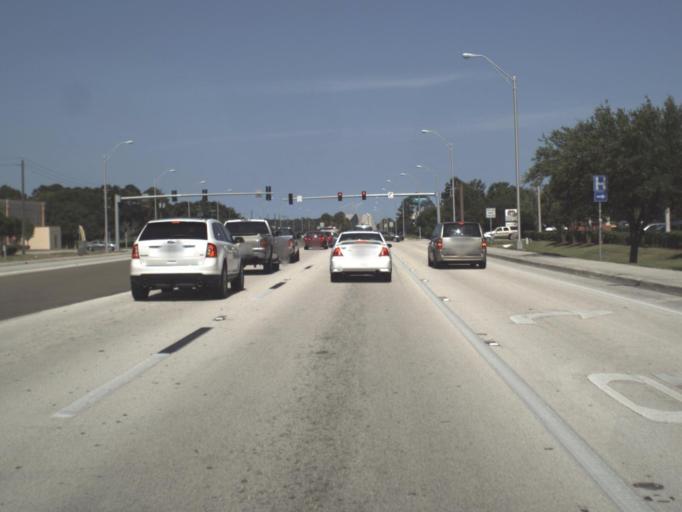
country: US
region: Florida
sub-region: Saint Johns County
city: Saint Augustine South
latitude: 29.8668
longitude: -81.3199
